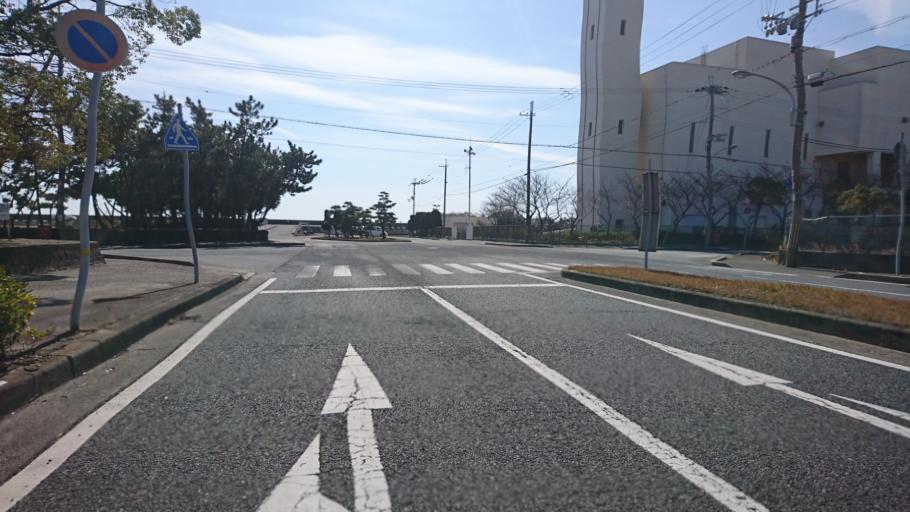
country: JP
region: Hyogo
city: Kakogawacho-honmachi
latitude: 34.6961
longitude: 134.8498
